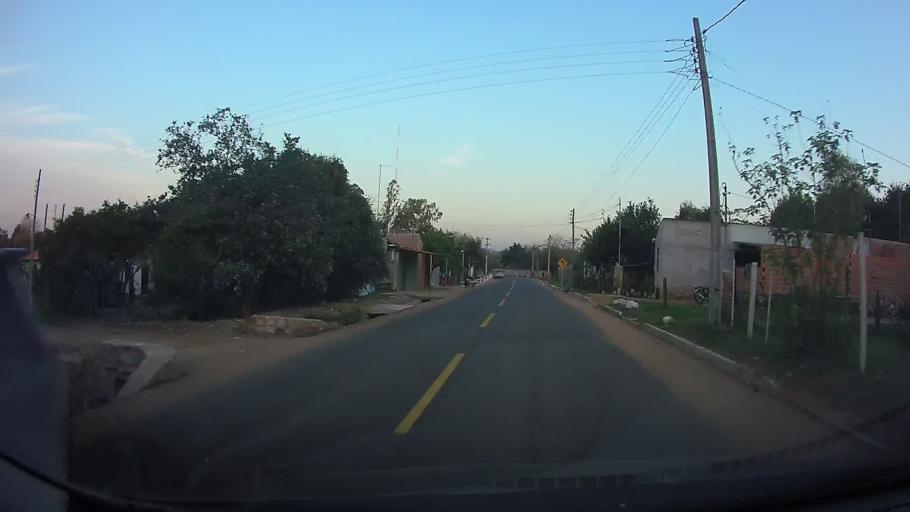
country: PY
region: Central
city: Limpio
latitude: -25.2434
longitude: -57.4939
